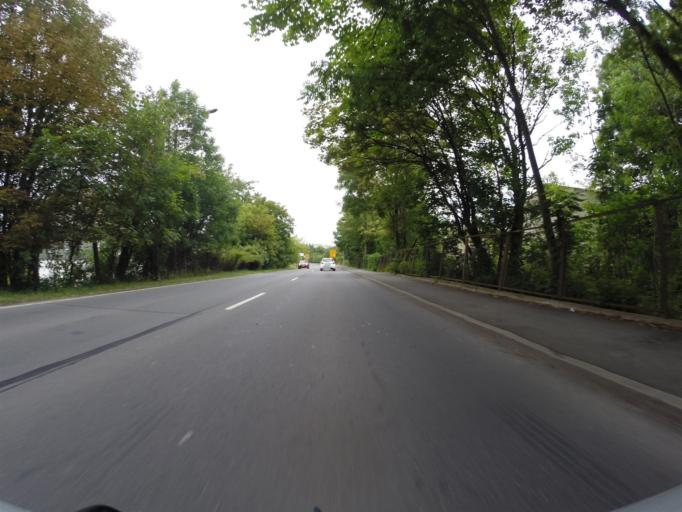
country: DE
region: Thuringia
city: Greussen
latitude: 51.2214
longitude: 10.9478
